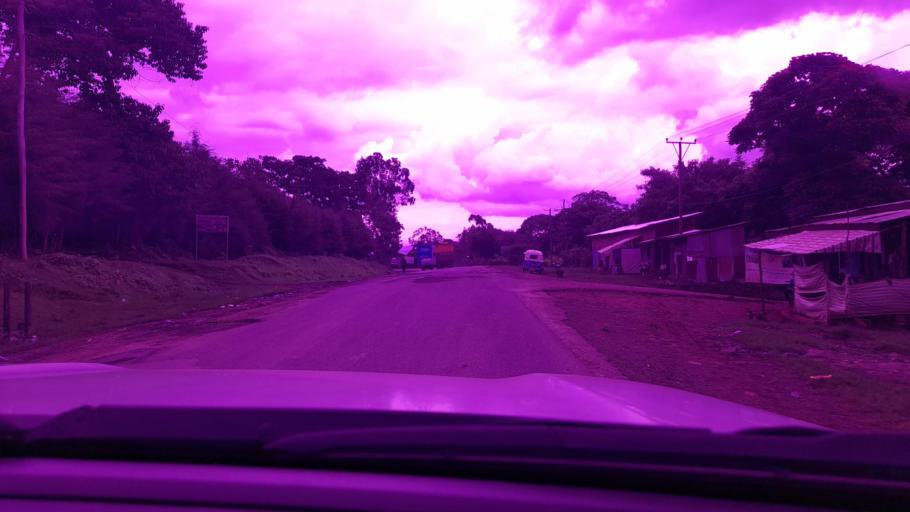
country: ET
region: Oromiya
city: Jima
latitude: 7.6658
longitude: 36.8722
